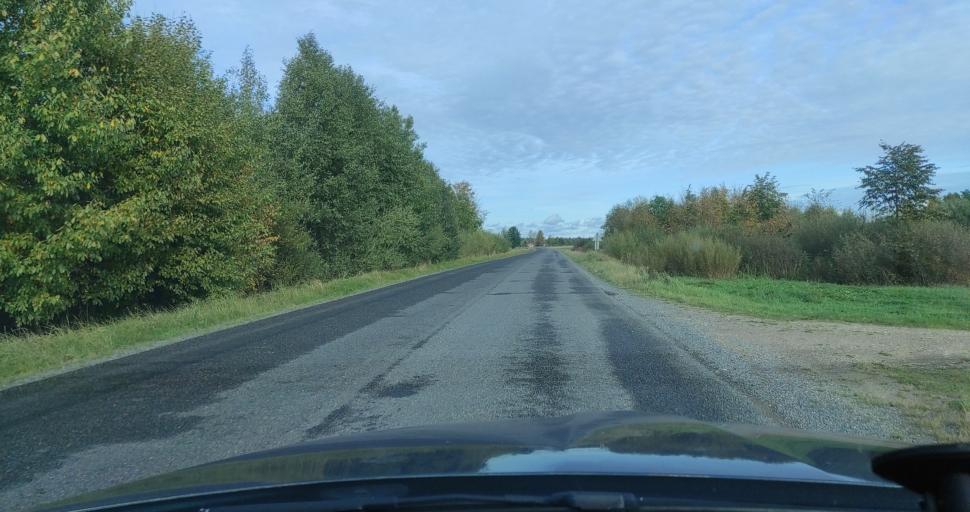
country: LV
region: Jaunpils
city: Jaunpils
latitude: 56.6916
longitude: 22.9770
